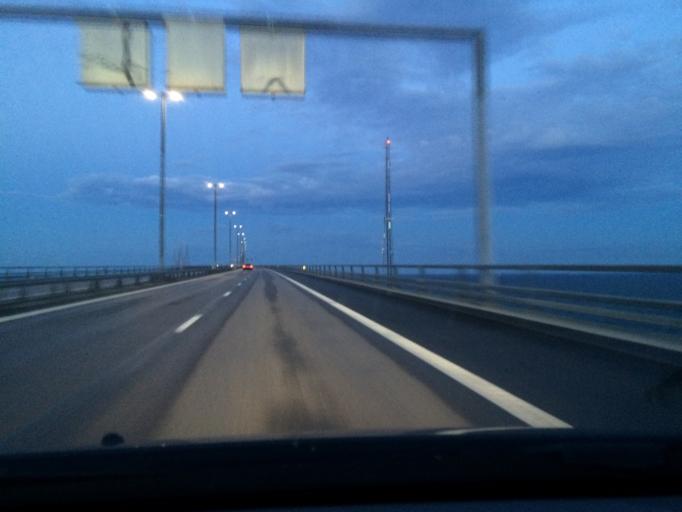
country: DK
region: Capital Region
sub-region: Dragor Kommune
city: Dragor
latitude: 55.5903
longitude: 12.7735
